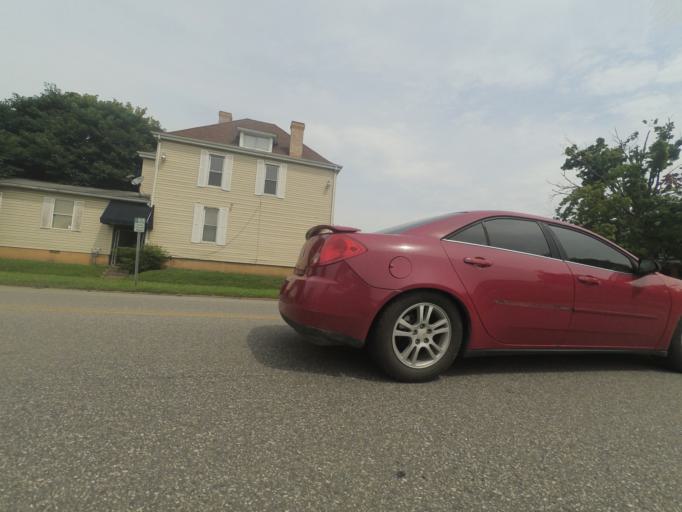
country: US
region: West Virginia
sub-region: Cabell County
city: Huntington
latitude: 38.4157
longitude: -82.4481
